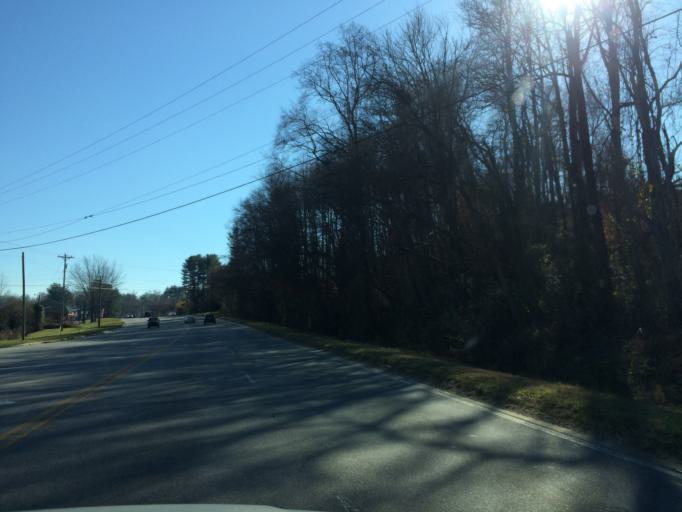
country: US
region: North Carolina
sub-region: Henderson County
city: Mills River
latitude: 35.3912
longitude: -82.5682
